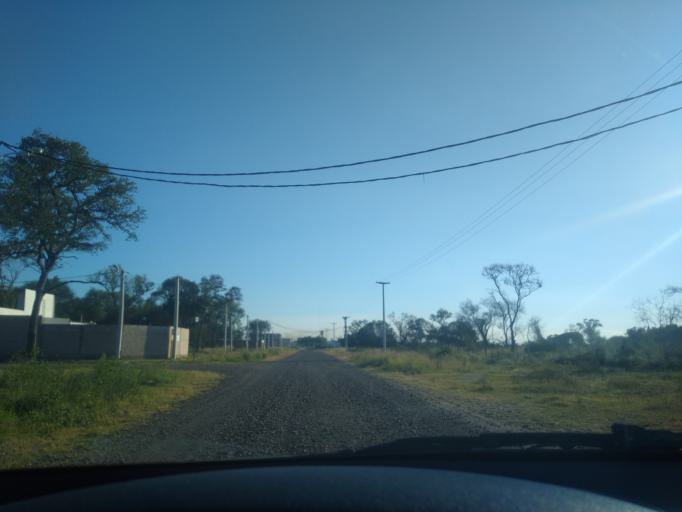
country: AR
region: Chaco
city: Resistencia
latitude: -27.4102
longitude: -58.9551
